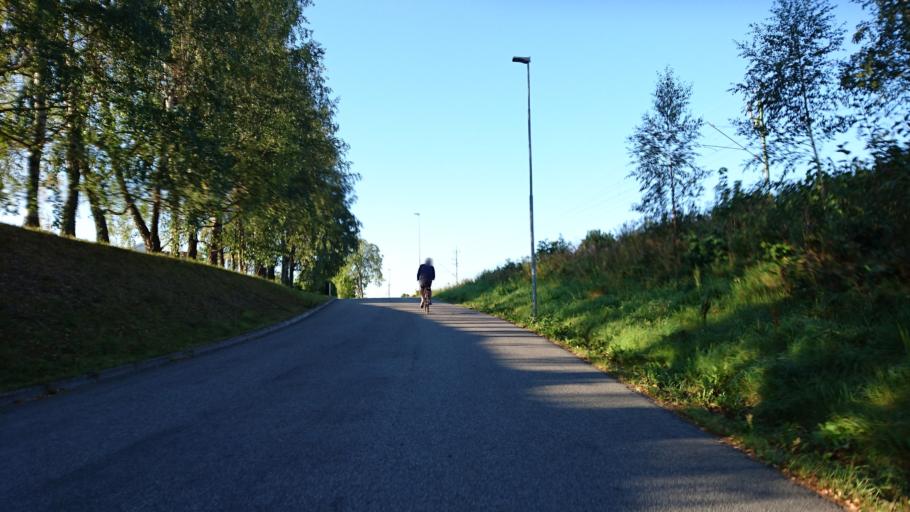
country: SE
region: Joenkoeping
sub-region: Jonkopings Kommun
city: Jonkoping
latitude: 57.8034
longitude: 14.1512
